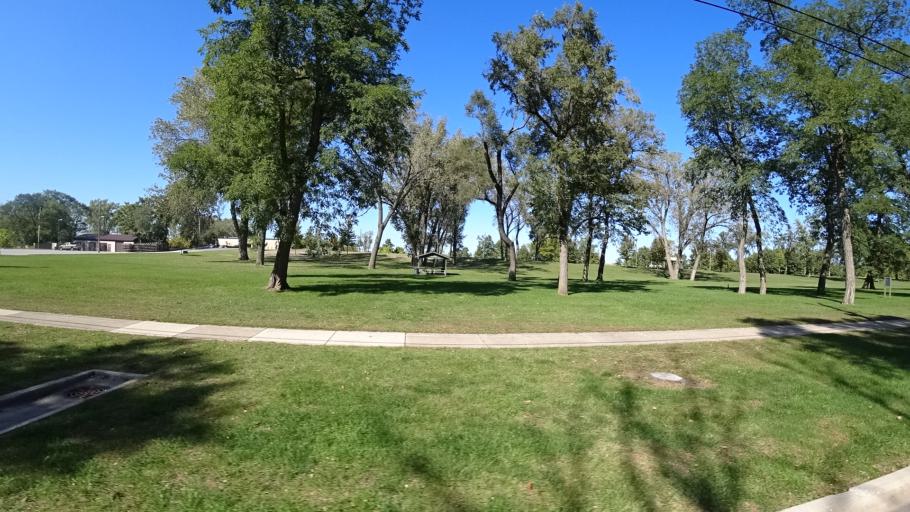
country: US
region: Indiana
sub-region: LaPorte County
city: Michigan City
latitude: 41.7269
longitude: -86.8975
